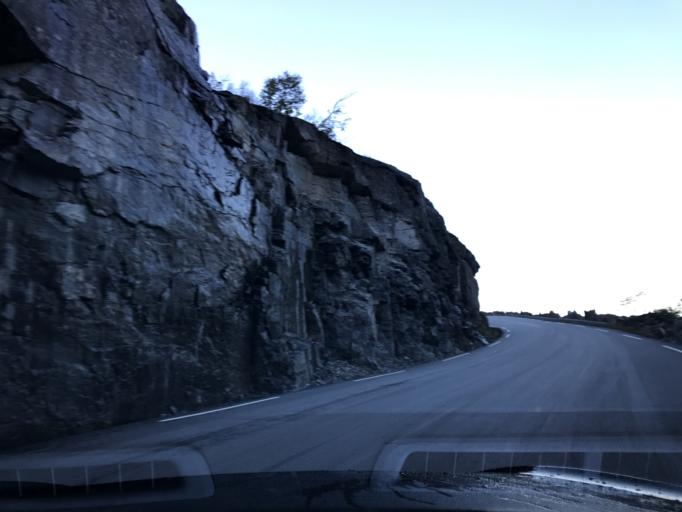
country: NO
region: More og Romsdal
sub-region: Rauma
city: Andalsnes
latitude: 62.4561
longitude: 7.6702
